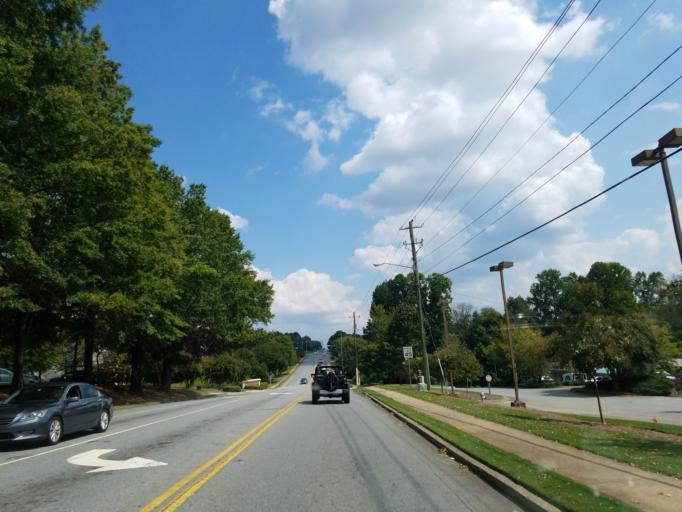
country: US
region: Georgia
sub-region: Fulton County
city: Alpharetta
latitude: 34.0609
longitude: -84.3240
